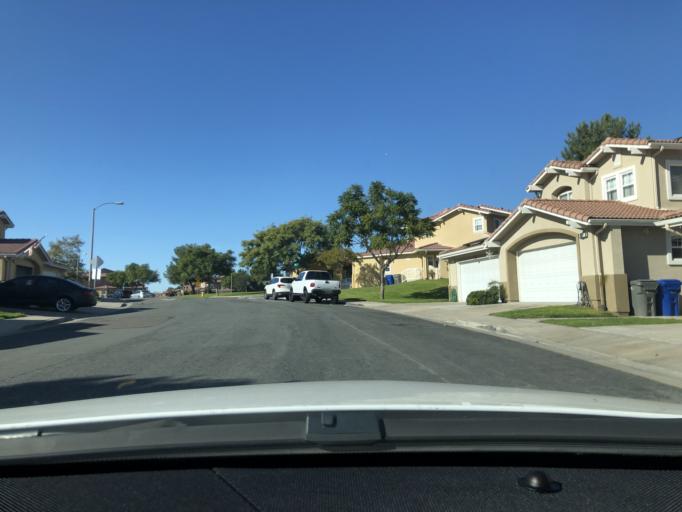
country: US
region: California
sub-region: San Diego County
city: Lemon Grove
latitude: 32.7392
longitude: -117.0630
